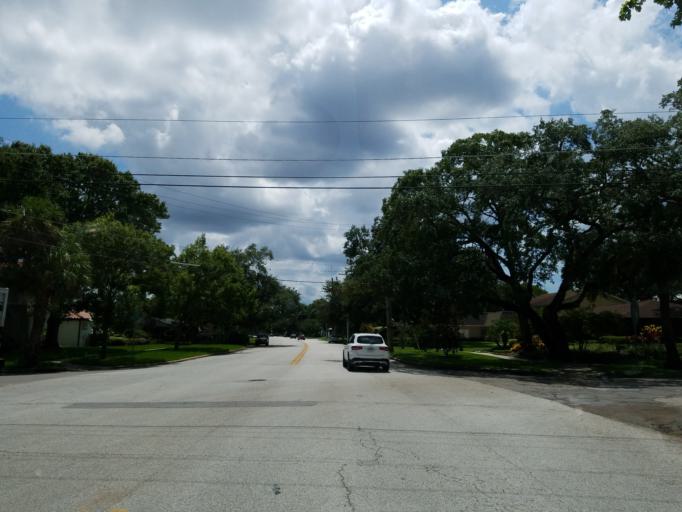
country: US
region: Florida
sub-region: Hillsborough County
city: Tampa
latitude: 27.9246
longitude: -82.4586
